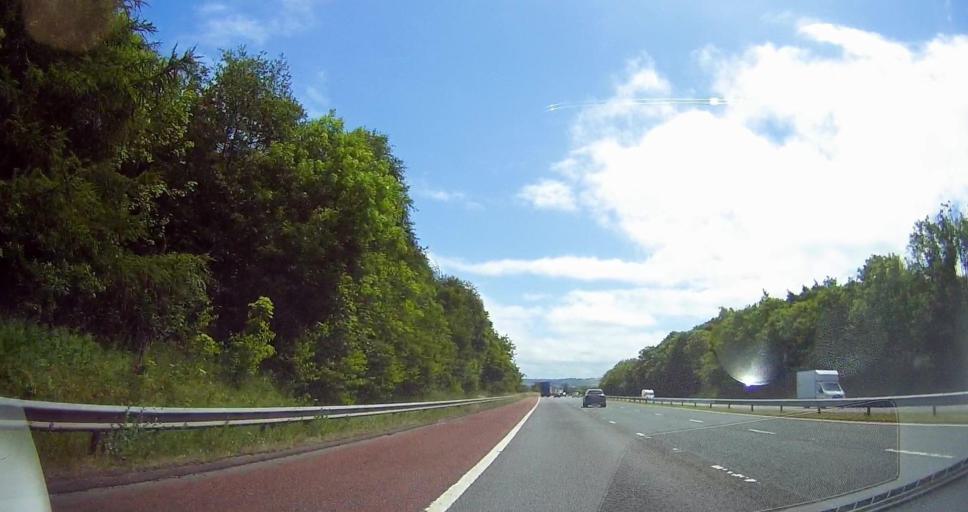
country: GB
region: England
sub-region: Cumbria
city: Penrith
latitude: 54.7623
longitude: -2.8333
